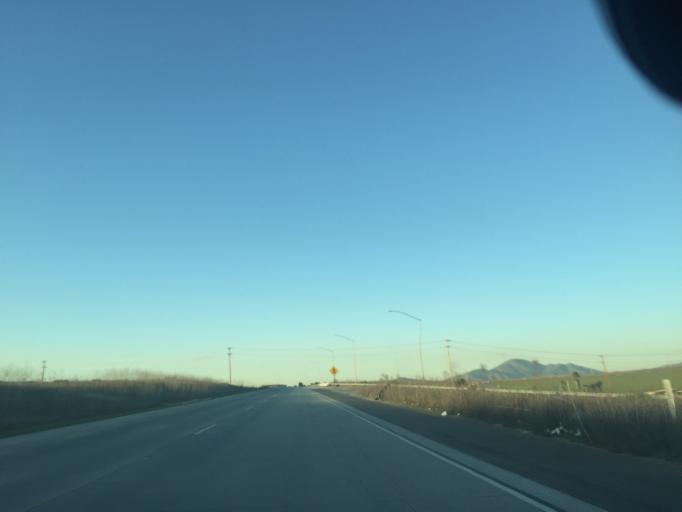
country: MX
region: Baja California
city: Tijuana
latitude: 32.5653
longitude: -116.9477
